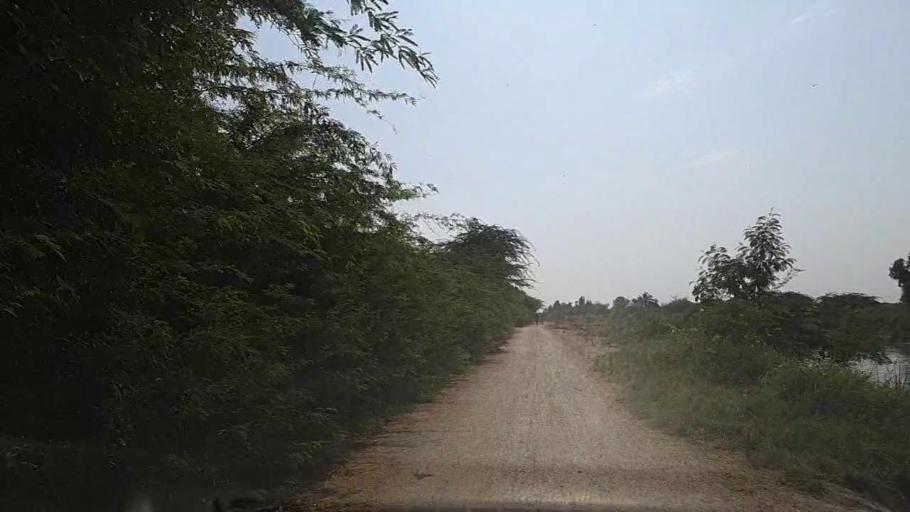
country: PK
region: Sindh
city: Thatta
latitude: 24.7916
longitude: 67.8293
